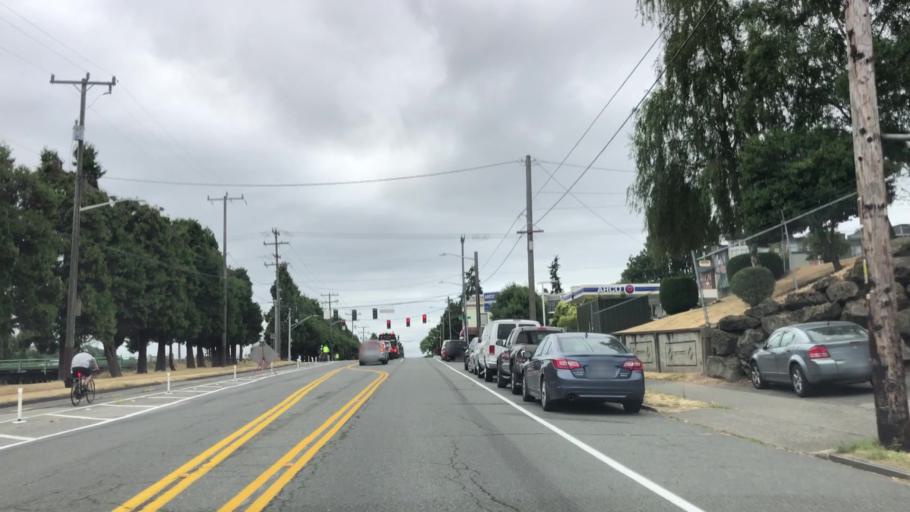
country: US
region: Washington
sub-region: King County
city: Seattle
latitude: 47.6495
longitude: -122.3822
